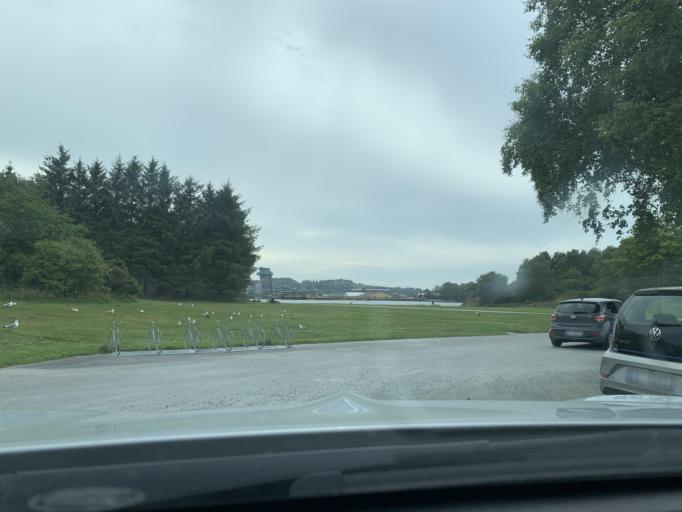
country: NO
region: Rogaland
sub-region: Stavanger
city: Stavanger
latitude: 58.9251
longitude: 5.7472
